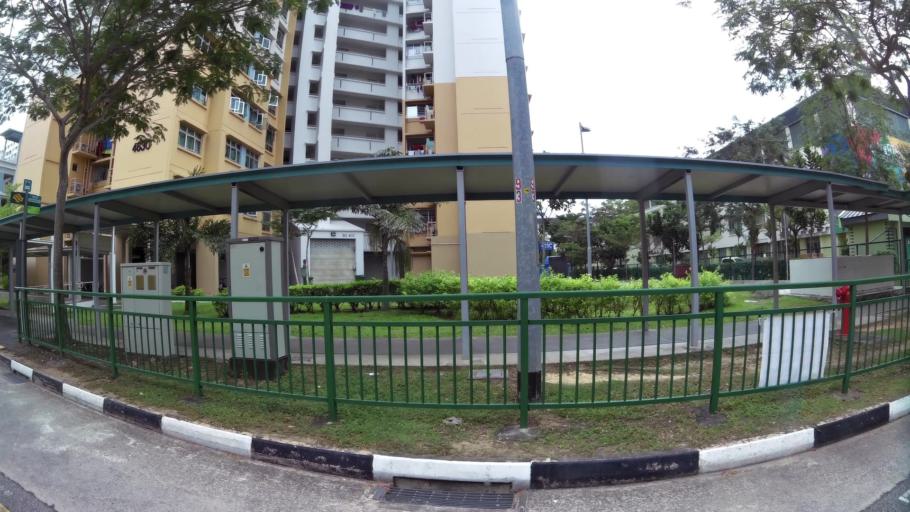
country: MY
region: Johor
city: Johor Bahru
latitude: 1.4564
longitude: 103.8146
